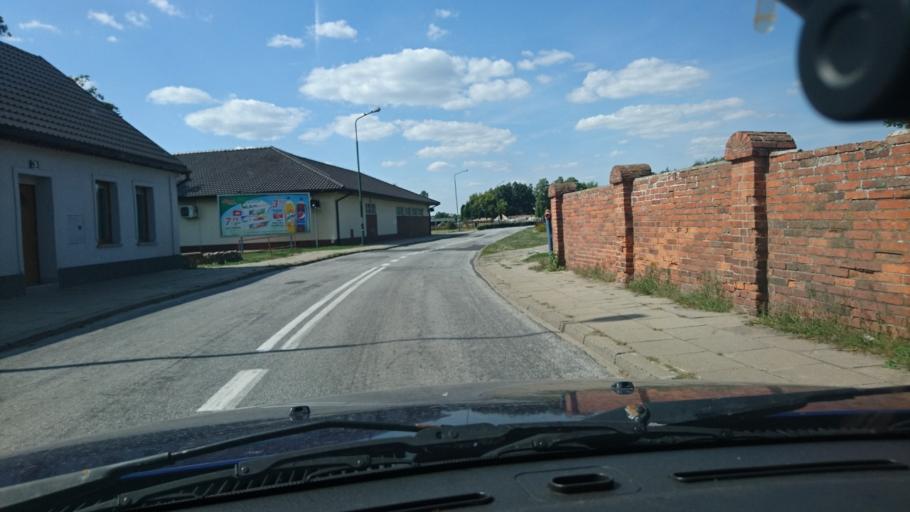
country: PL
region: Greater Poland Voivodeship
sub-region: Powiat krotoszynski
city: Sulmierzyce
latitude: 51.6066
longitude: 17.5256
